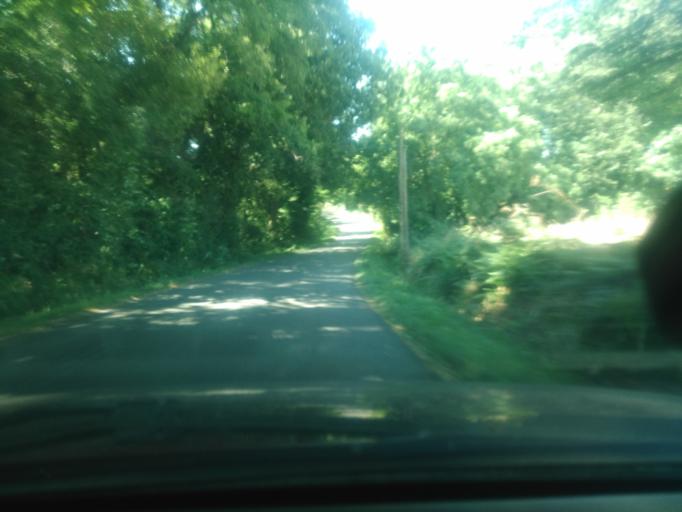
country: FR
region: Pays de la Loire
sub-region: Departement de la Vendee
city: Dompierre-sur-Yon
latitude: 46.7212
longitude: -1.3670
